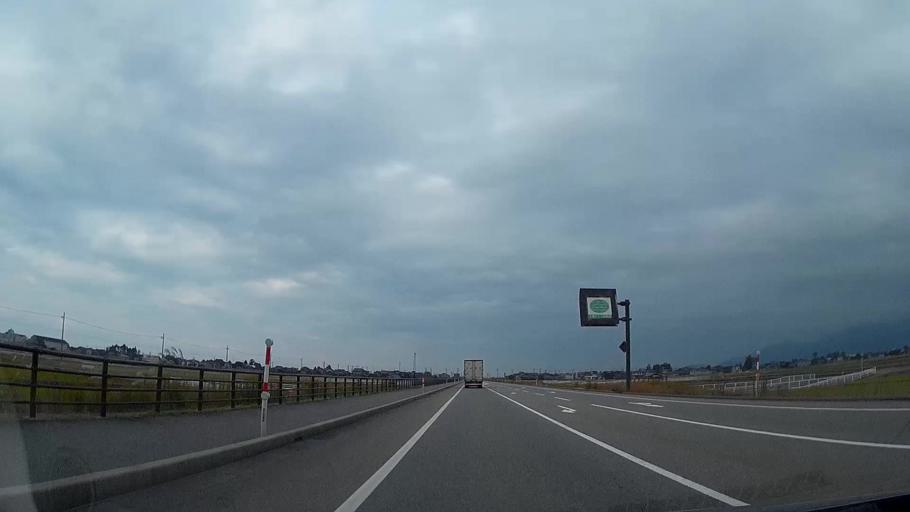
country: JP
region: Toyama
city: Nyuzen
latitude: 36.9168
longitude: 137.4625
